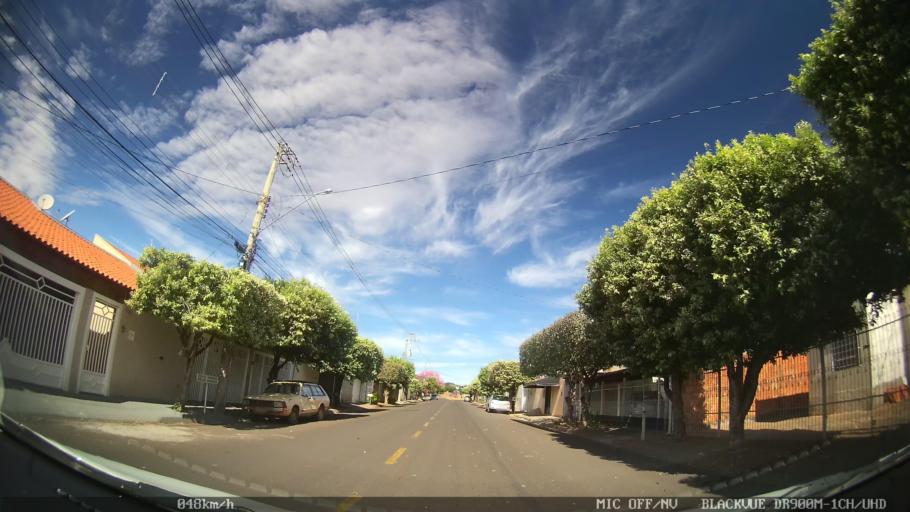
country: BR
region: Sao Paulo
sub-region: Bady Bassitt
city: Bady Bassitt
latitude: -20.8296
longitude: -49.4962
